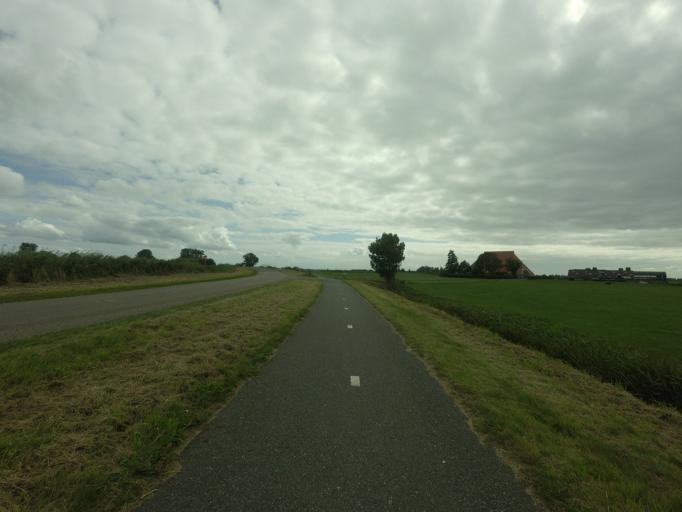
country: NL
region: Friesland
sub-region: Sudwest Fryslan
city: Heeg
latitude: 52.9832
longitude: 5.5403
